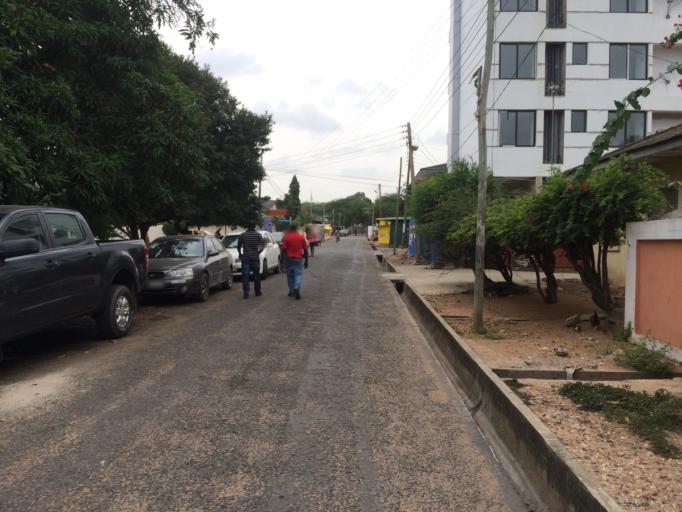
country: GH
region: Greater Accra
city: Accra
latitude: 5.5574
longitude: -0.1830
